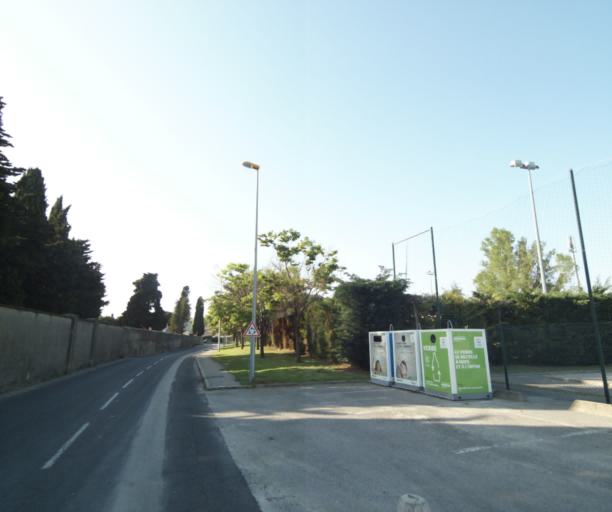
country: FR
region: Languedoc-Roussillon
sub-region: Departement de l'Herault
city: Juvignac
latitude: 43.6058
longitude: 3.7849
